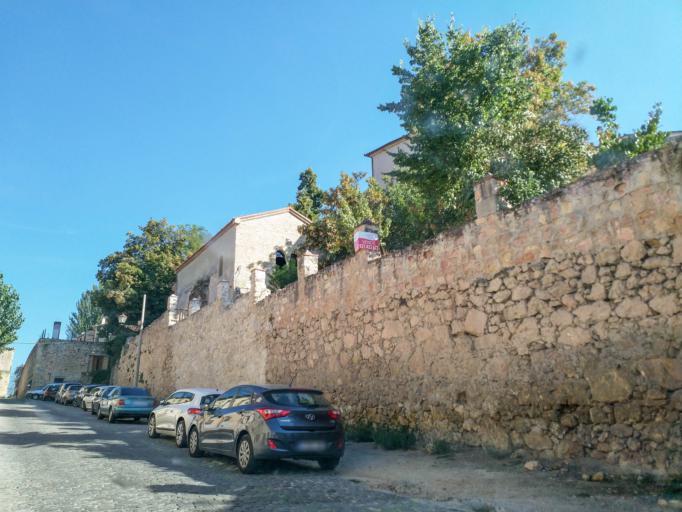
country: ES
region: Castille and Leon
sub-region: Provincia de Segovia
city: Segovia
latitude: 40.9531
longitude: -4.1263
